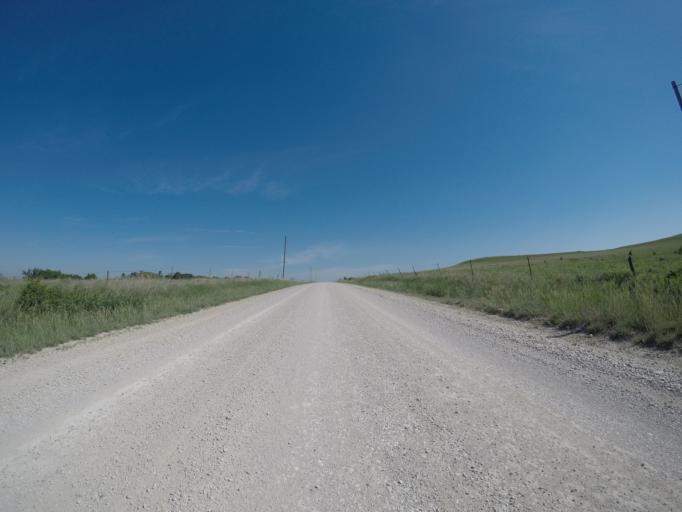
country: US
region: Kansas
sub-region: Wabaunsee County
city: Alma
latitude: 39.0020
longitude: -96.1137
